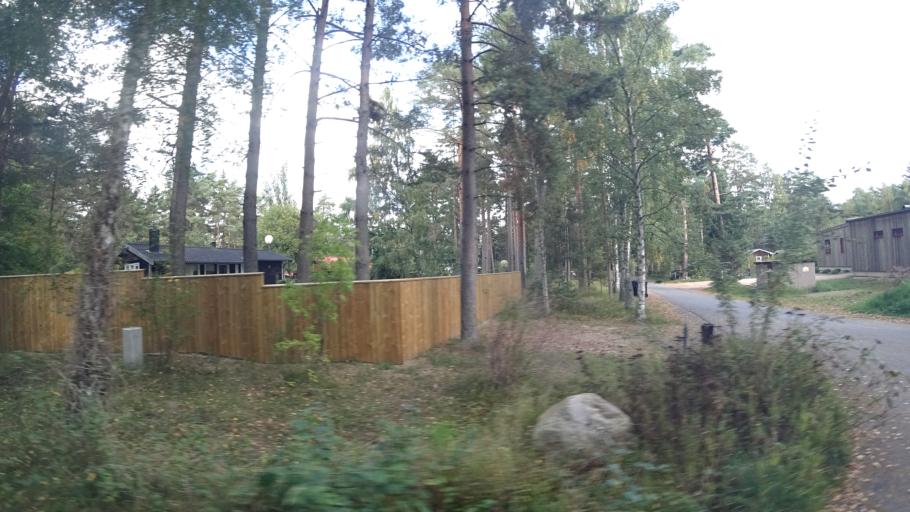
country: SE
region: Skane
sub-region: Kristianstads Kommun
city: Ahus
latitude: 55.9108
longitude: 14.2982
